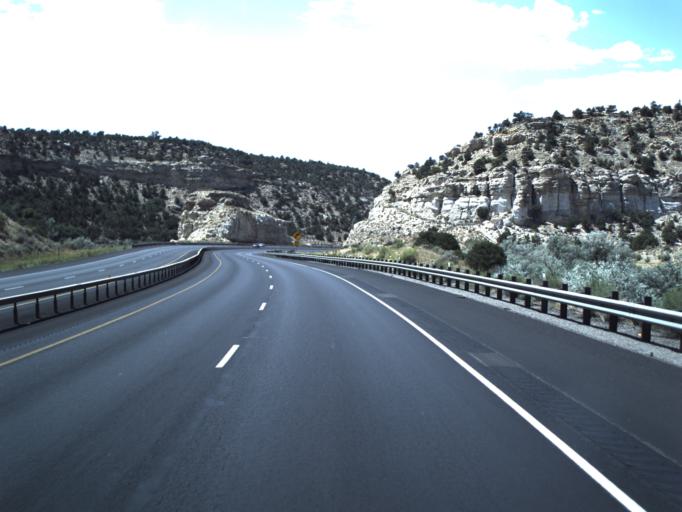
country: US
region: Utah
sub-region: Sevier County
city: Salina
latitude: 38.9098
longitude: -111.7044
